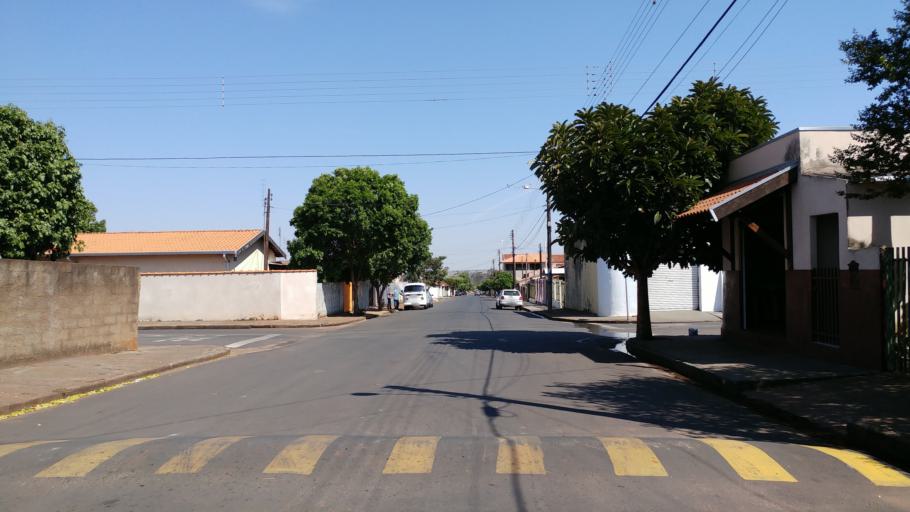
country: BR
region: Sao Paulo
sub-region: Paraguacu Paulista
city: Paraguacu Paulista
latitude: -22.4255
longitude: -50.5847
